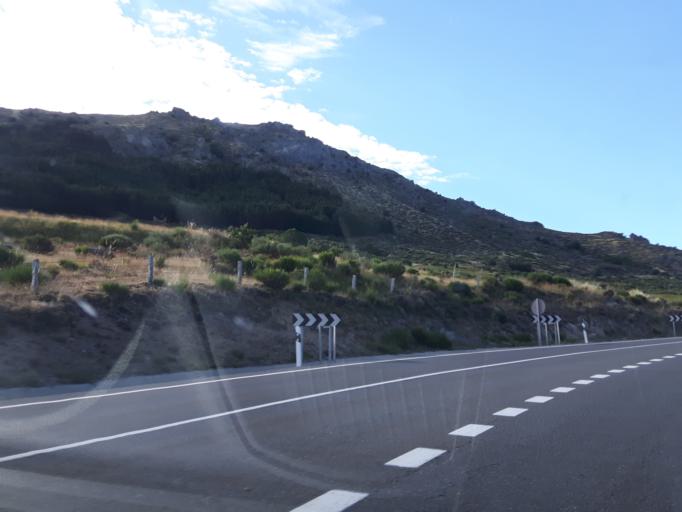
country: ES
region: Castille and Leon
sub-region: Provincia de Avila
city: Mengamunoz
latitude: 40.4871
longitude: -5.0091
